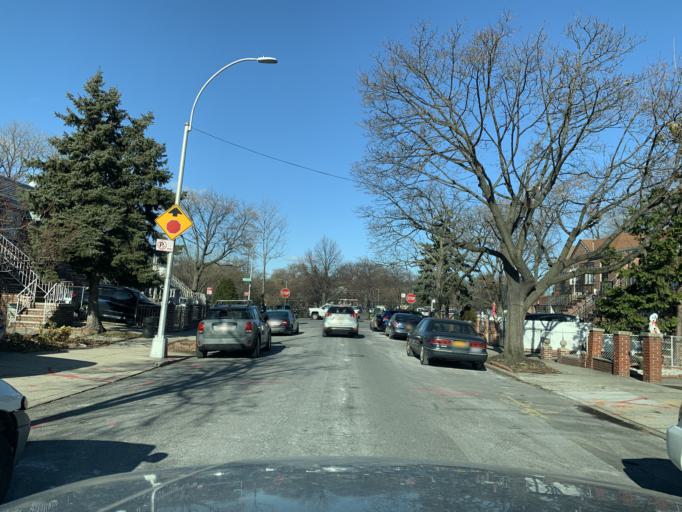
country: US
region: New York
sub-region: Queens County
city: Long Island City
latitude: 40.7615
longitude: -73.8959
